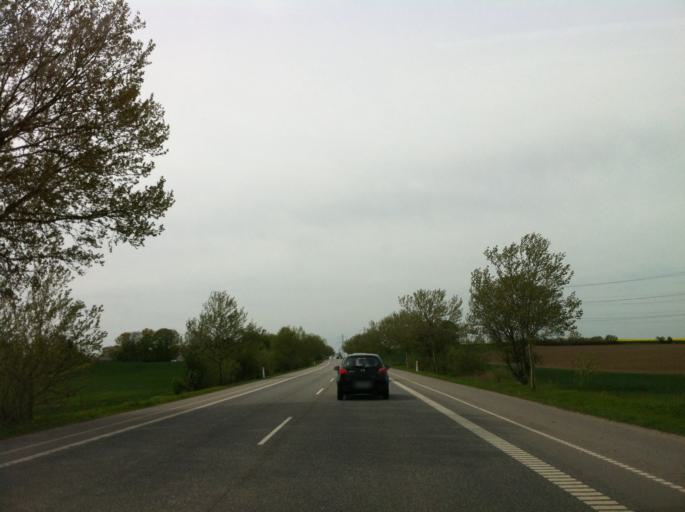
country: DK
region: Capital Region
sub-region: Frederikssund Kommune
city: Slangerup
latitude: 55.8598
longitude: 12.1677
